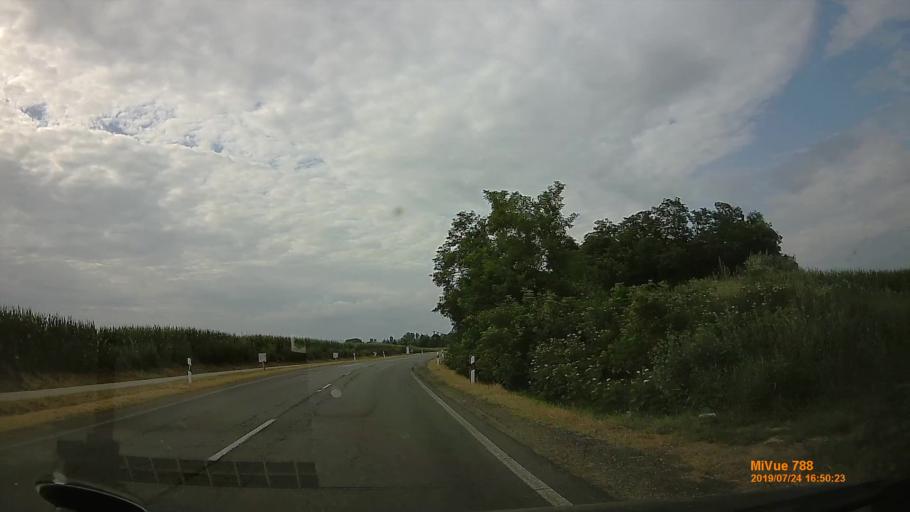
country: HU
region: Szabolcs-Szatmar-Bereg
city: Tiszanagyfalu
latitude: 48.1033
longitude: 21.4900
